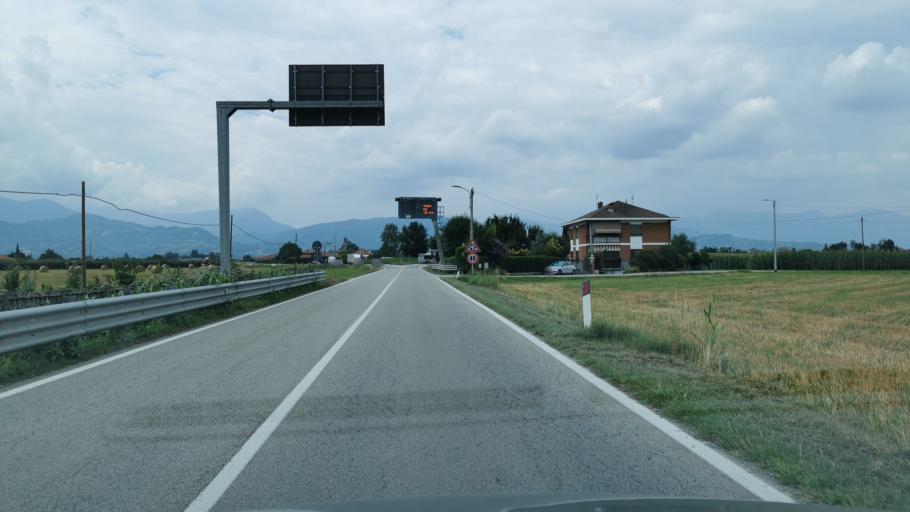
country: IT
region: Piedmont
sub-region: Provincia di Torino
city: Osasco
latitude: 44.8419
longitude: 7.3531
